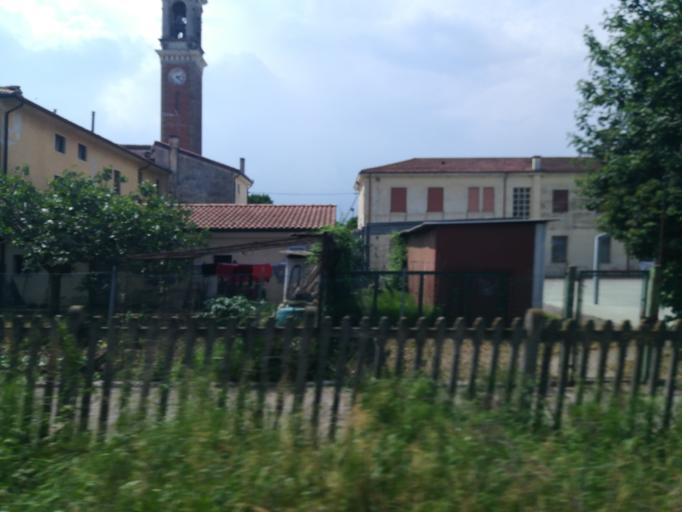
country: IT
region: Veneto
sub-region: Provincia di Vicenza
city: Monticello Conte Otto
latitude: 45.6010
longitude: 11.5700
